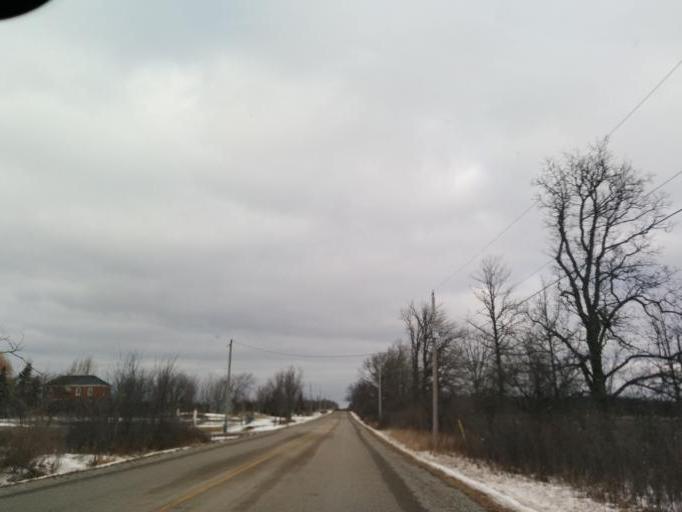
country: CA
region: Ontario
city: Brantford
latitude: 42.9933
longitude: -80.1342
